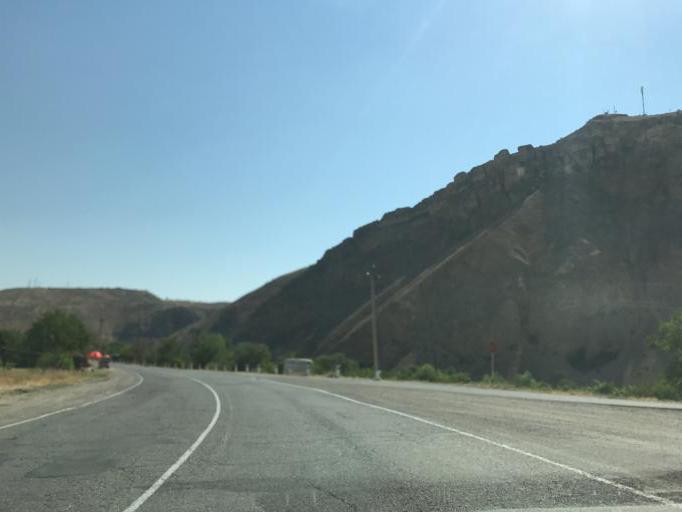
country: AM
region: Vayots' Dzori Marz
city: Areni
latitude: 39.7273
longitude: 45.1902
